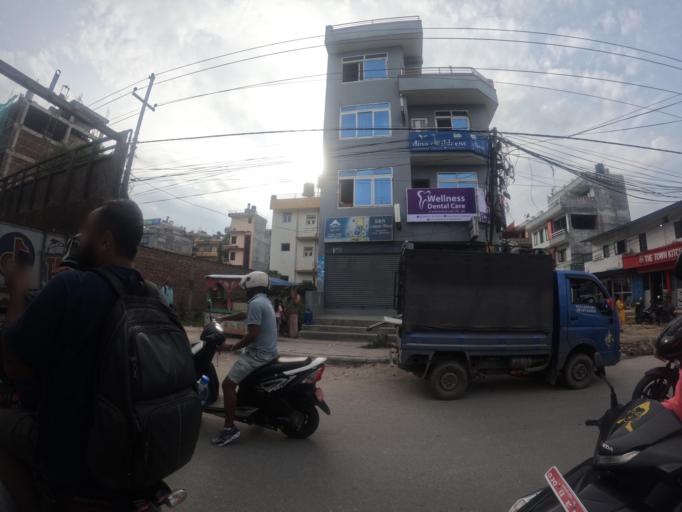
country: NP
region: Central Region
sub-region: Bagmati Zone
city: Bhaktapur
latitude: 27.6761
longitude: 85.3978
